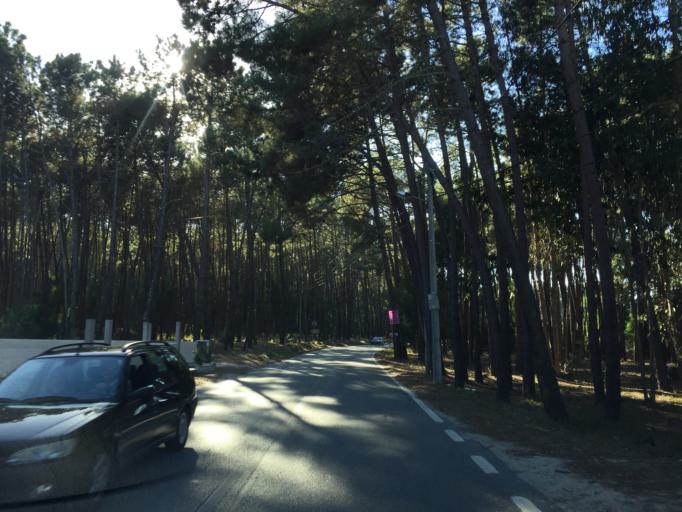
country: PT
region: Coimbra
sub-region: Figueira da Foz
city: Tavarede
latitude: 40.2156
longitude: -8.8646
